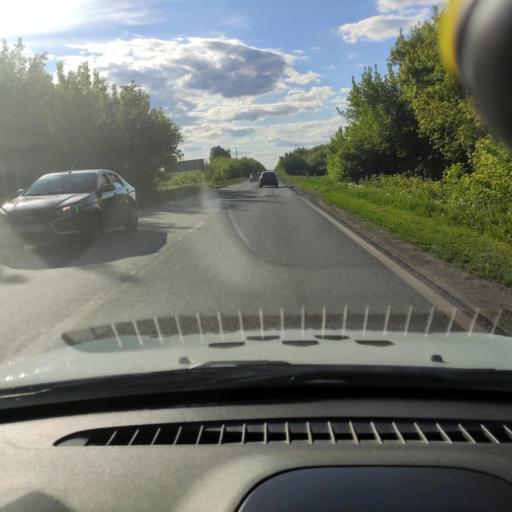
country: RU
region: Samara
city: Podstepki
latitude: 53.5680
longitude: 49.0941
